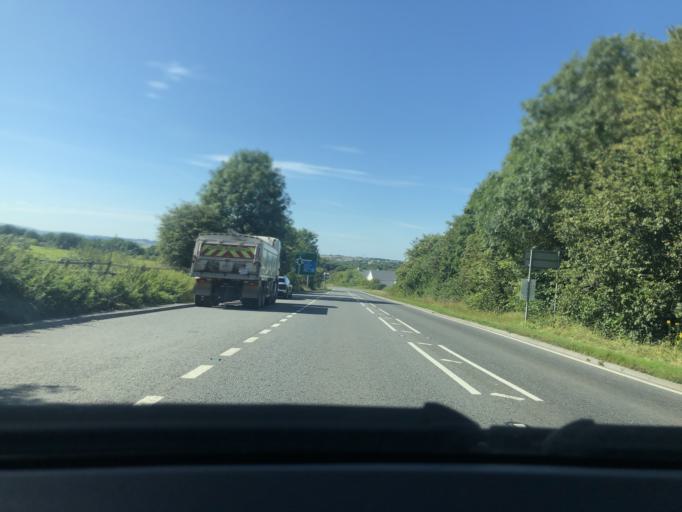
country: GB
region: England
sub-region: Somerset
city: Puriton
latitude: 51.1659
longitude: -2.9759
